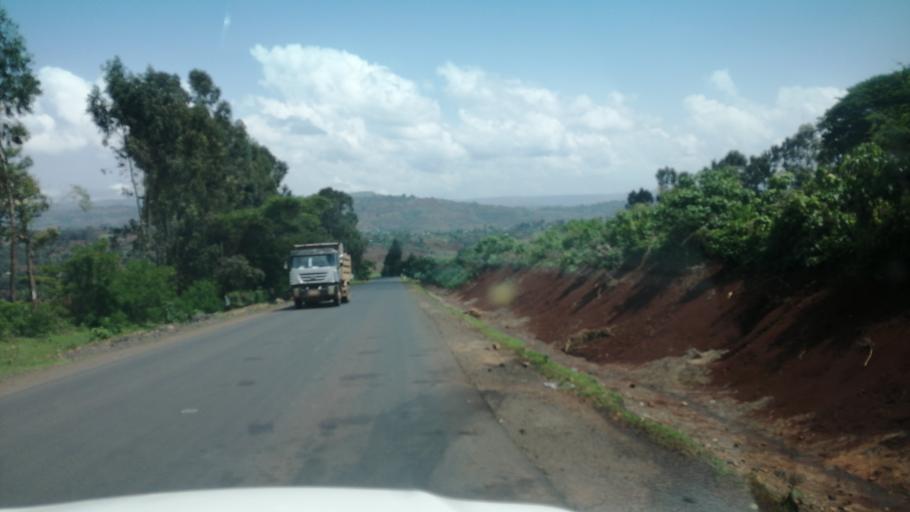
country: ET
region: Oromiya
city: Gedo
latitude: 8.9759
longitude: 37.5628
